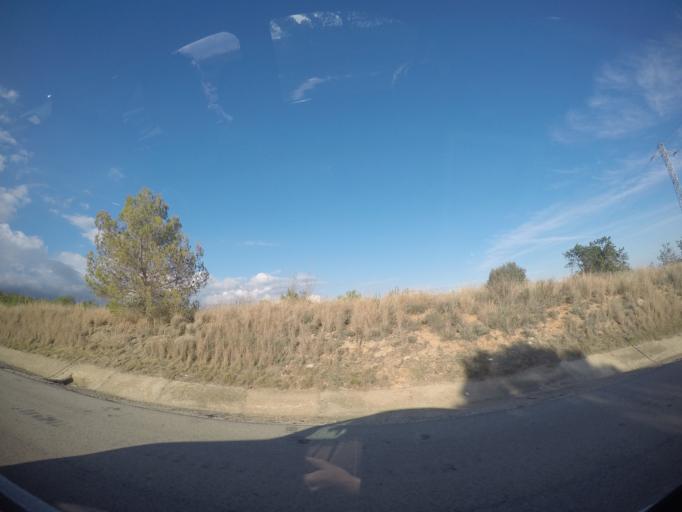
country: ES
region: Catalonia
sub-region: Provincia de Tarragona
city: la Bisbal del Penedes
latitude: 41.2811
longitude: 1.4977
